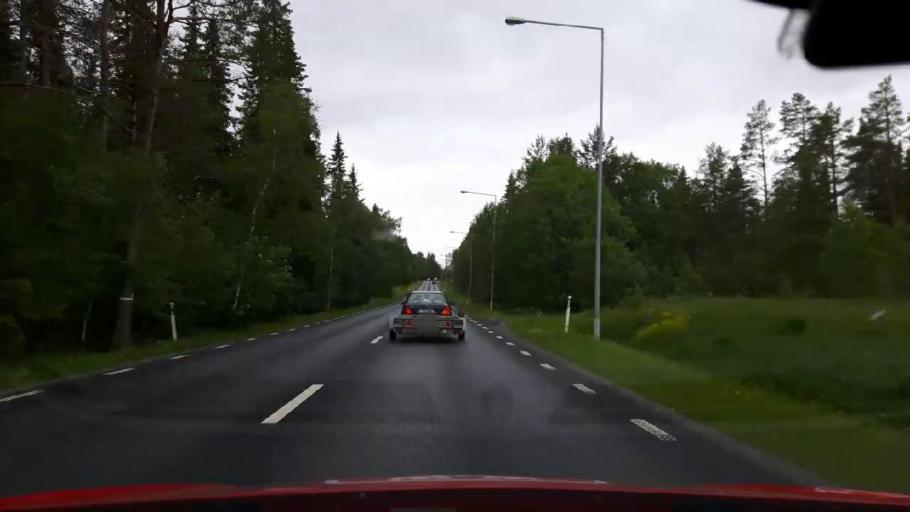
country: SE
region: Jaemtland
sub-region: OEstersunds Kommun
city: Ostersund
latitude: 63.1975
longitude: 14.6687
